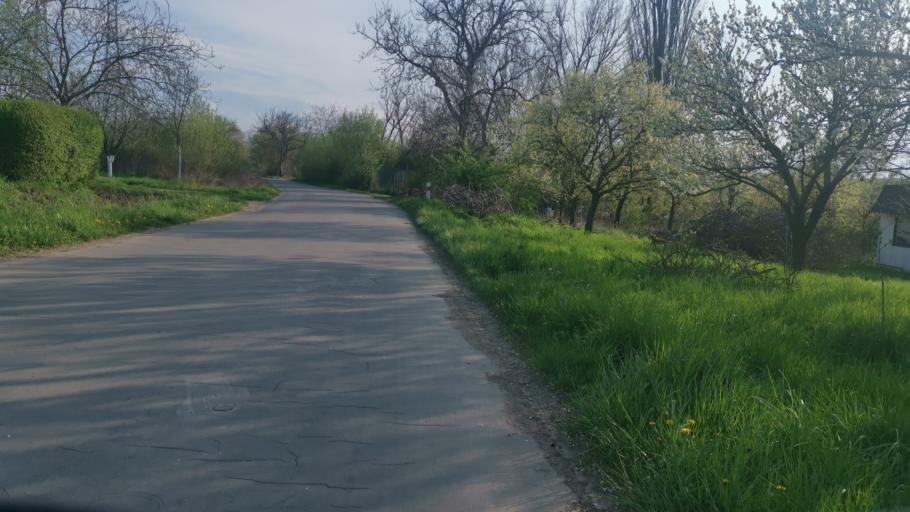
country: CZ
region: South Moravian
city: Petrov
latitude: 48.8567
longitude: 17.3069
